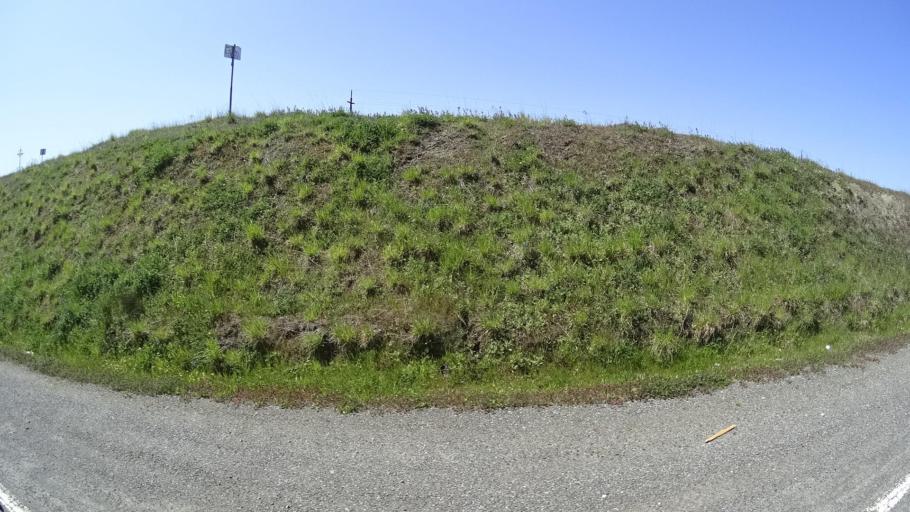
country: US
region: California
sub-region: Humboldt County
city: Redway
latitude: 40.1004
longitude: -123.6864
